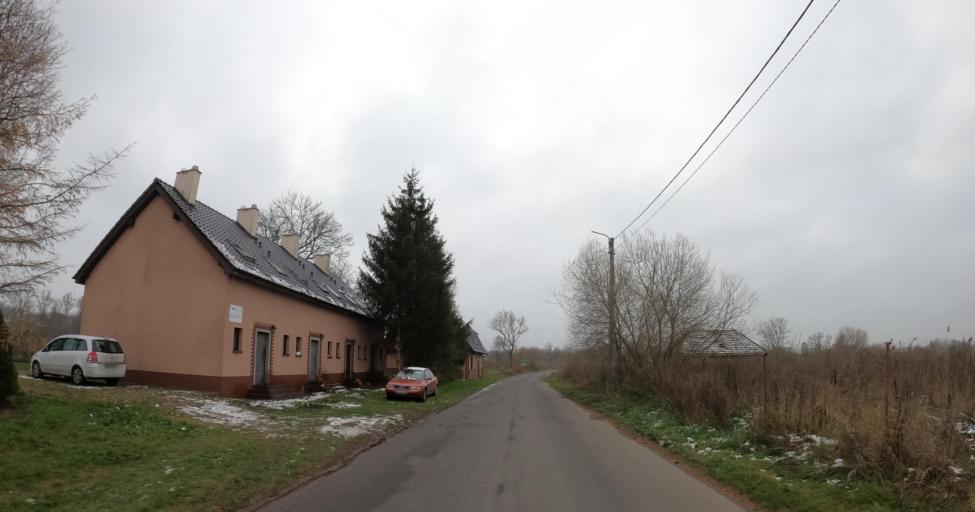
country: PL
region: West Pomeranian Voivodeship
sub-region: Powiat bialogardzki
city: Karlino
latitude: 53.9822
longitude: 15.8954
